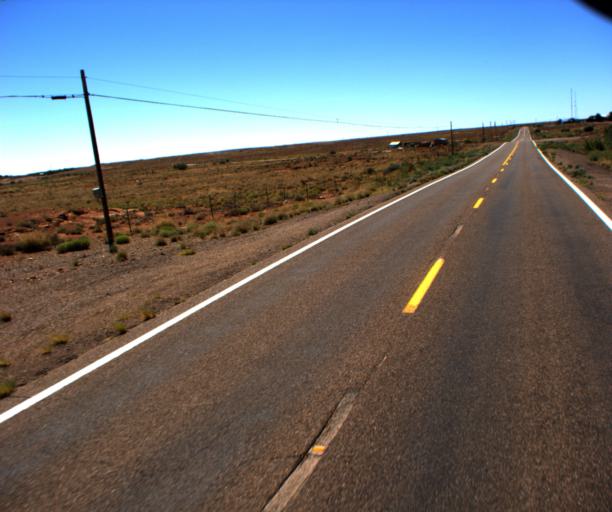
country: US
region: Arizona
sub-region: Navajo County
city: Winslow
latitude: 34.9858
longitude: -110.6631
